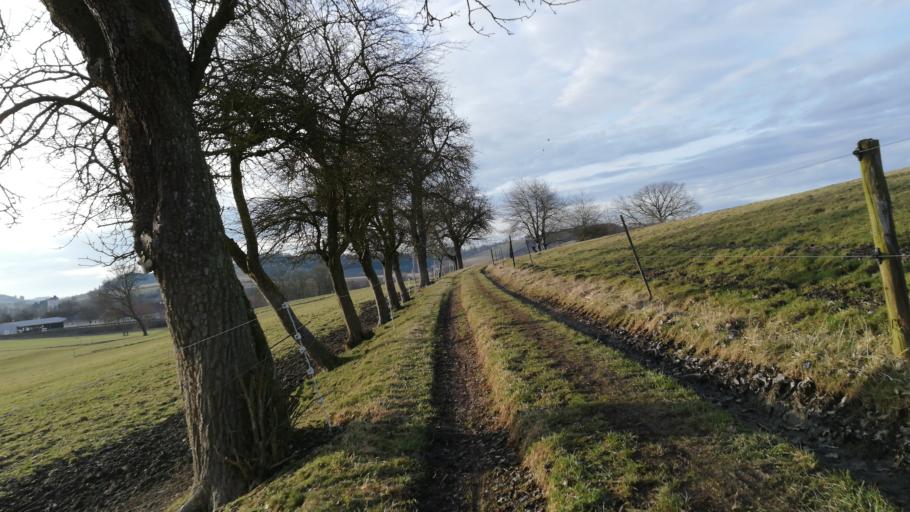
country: AT
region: Upper Austria
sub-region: Politischer Bezirk Grieskirchen
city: Bad Schallerbach
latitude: 48.1963
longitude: 13.9325
